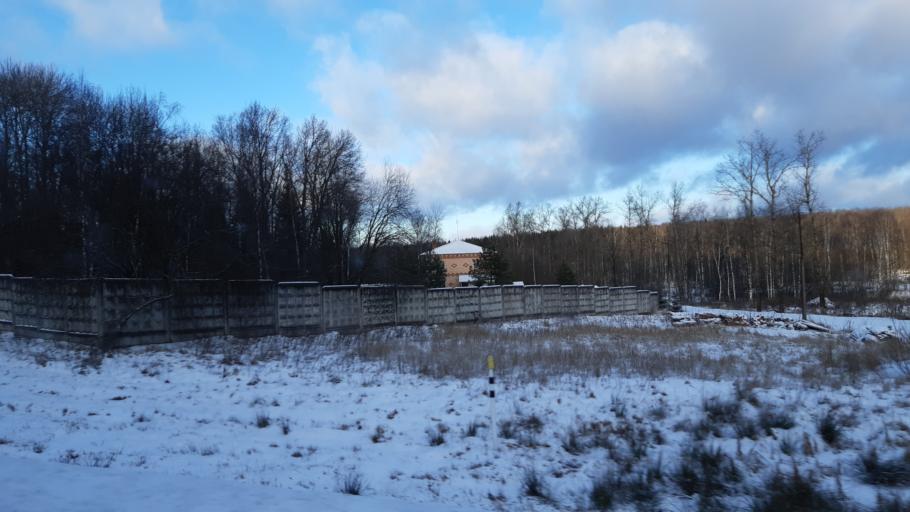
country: RU
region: Moskovskaya
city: Svatkovo
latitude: 56.3146
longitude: 38.3085
